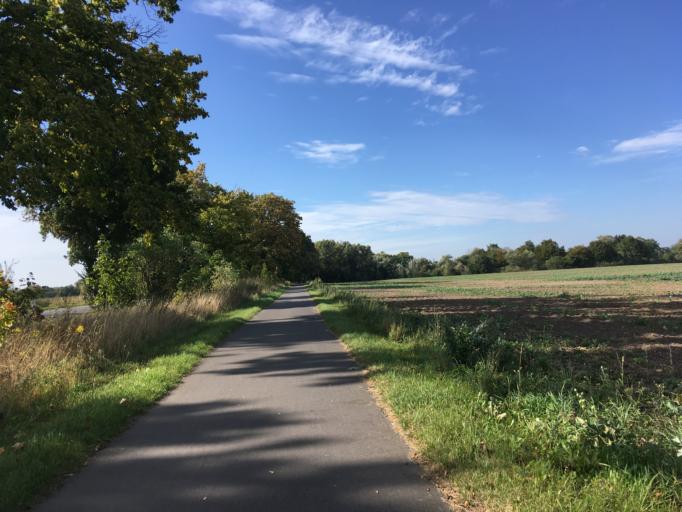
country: DE
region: Brandenburg
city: Altlandsberg
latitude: 52.5619
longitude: 13.7599
